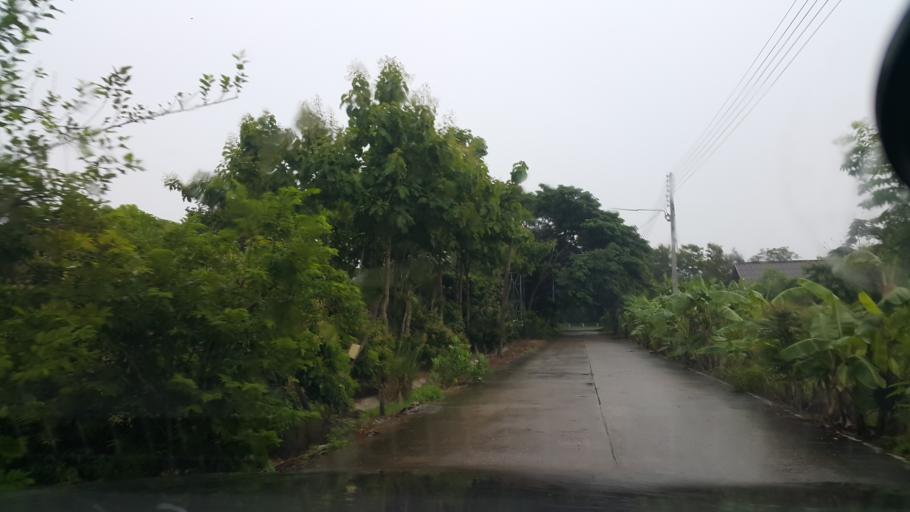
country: TH
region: Lamphun
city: Ban Thi
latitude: 18.6297
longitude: 99.1165
